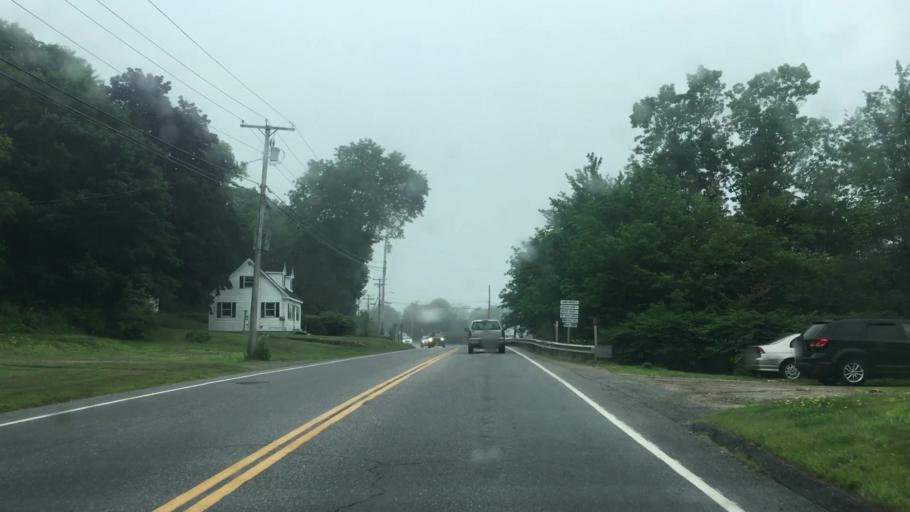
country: US
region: Maine
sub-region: Lincoln County
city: Boothbay
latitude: 43.8811
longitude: -69.6322
